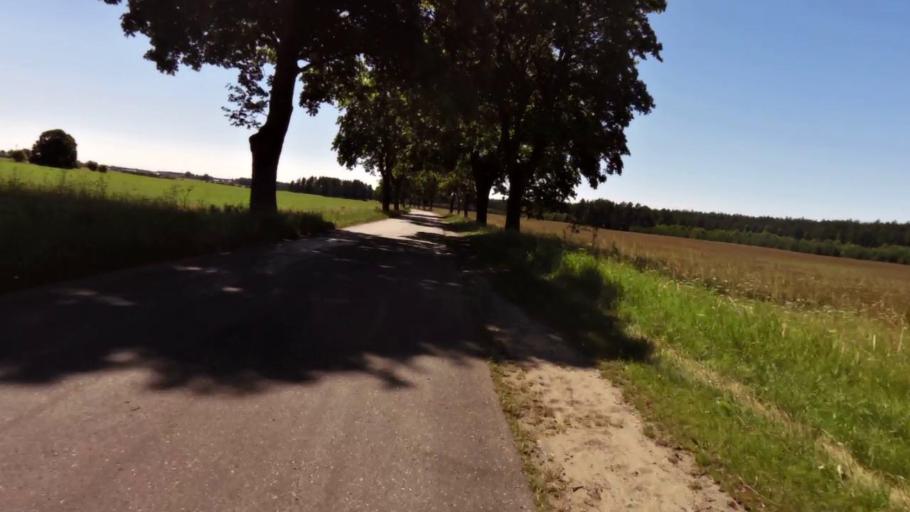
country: PL
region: West Pomeranian Voivodeship
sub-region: Powiat szczecinecki
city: Bialy Bor
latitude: 53.9186
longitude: 16.8402
